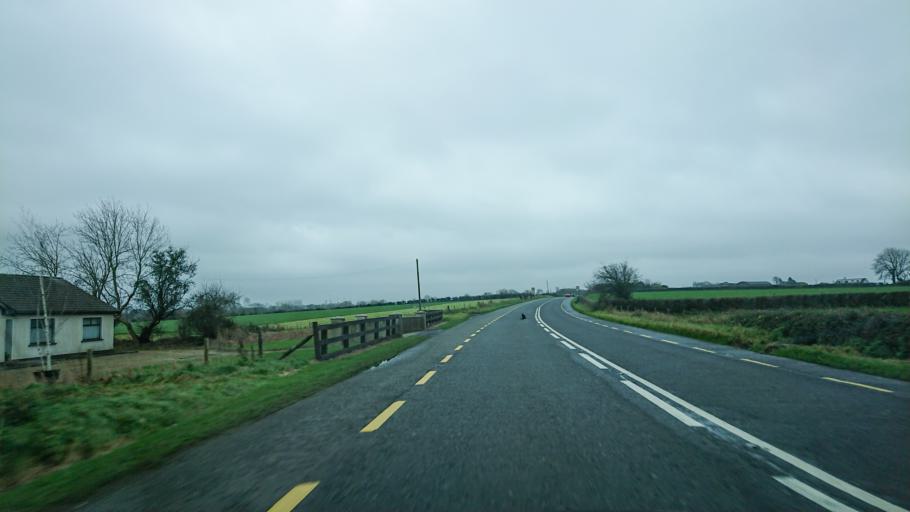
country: IE
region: Leinster
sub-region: Kilkenny
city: Mooncoin
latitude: 52.2905
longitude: -7.2387
